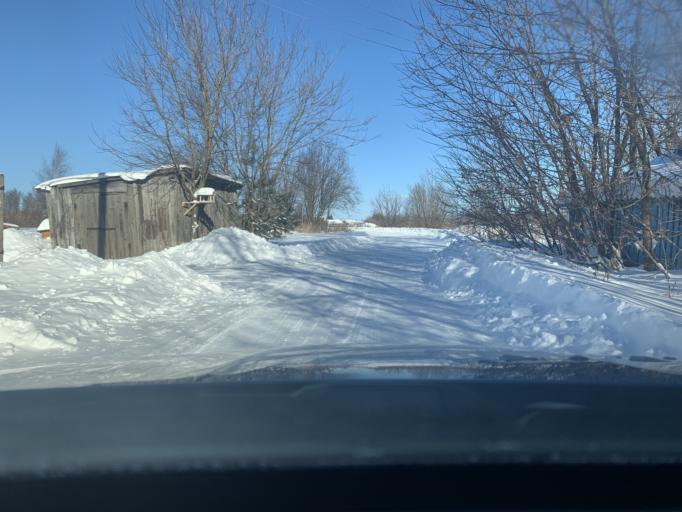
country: RU
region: Jaroslavl
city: Tunoshna
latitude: 57.6554
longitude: 40.0691
